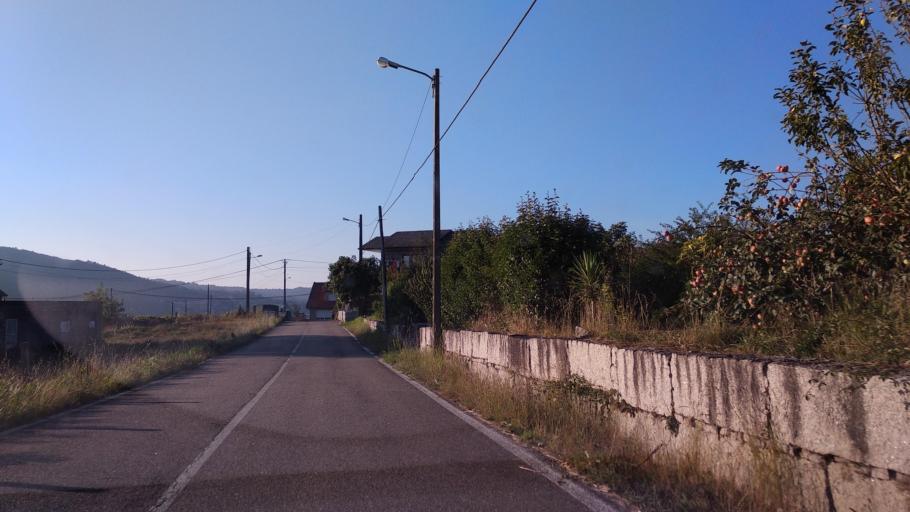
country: ES
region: Galicia
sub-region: Provincia de Pontevedra
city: Ponte Caldelas
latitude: 42.3626
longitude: -8.5314
